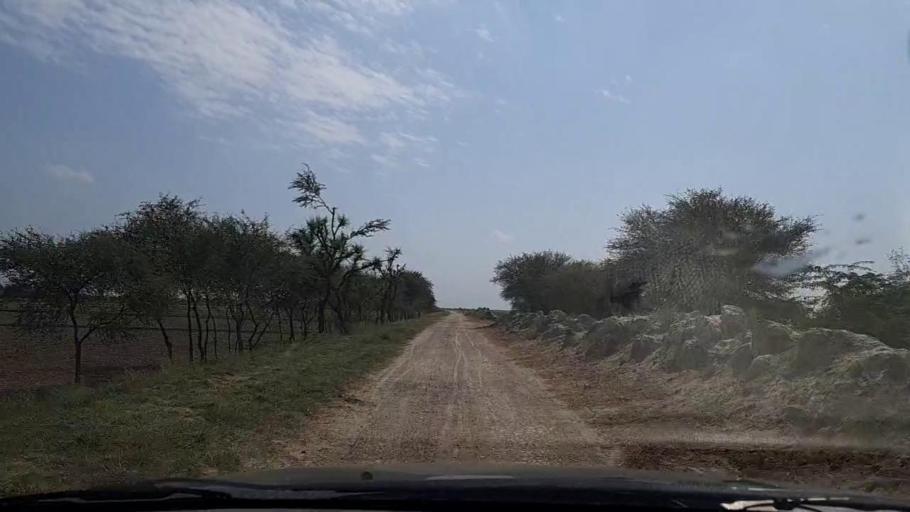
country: PK
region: Sindh
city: Mirpur Batoro
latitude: 24.5836
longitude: 68.1961
